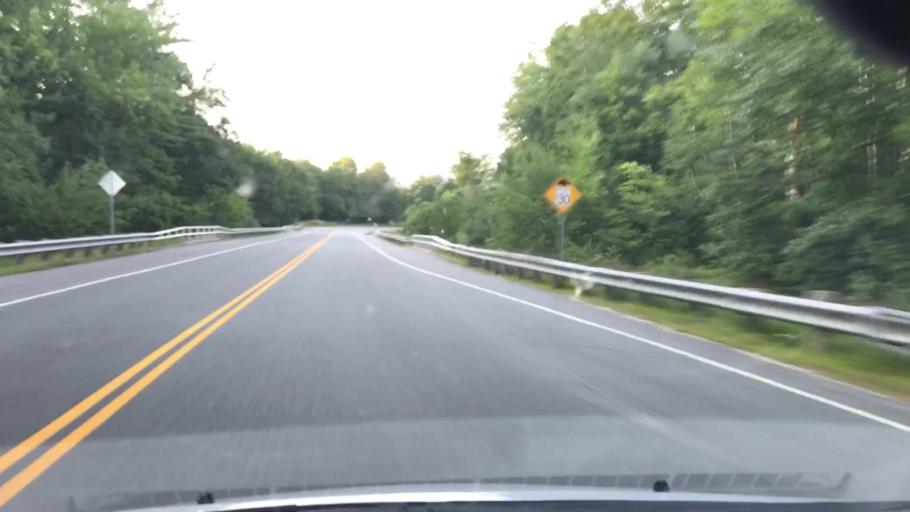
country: US
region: New Hampshire
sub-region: Grafton County
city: Rumney
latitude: 43.9080
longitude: -71.8889
